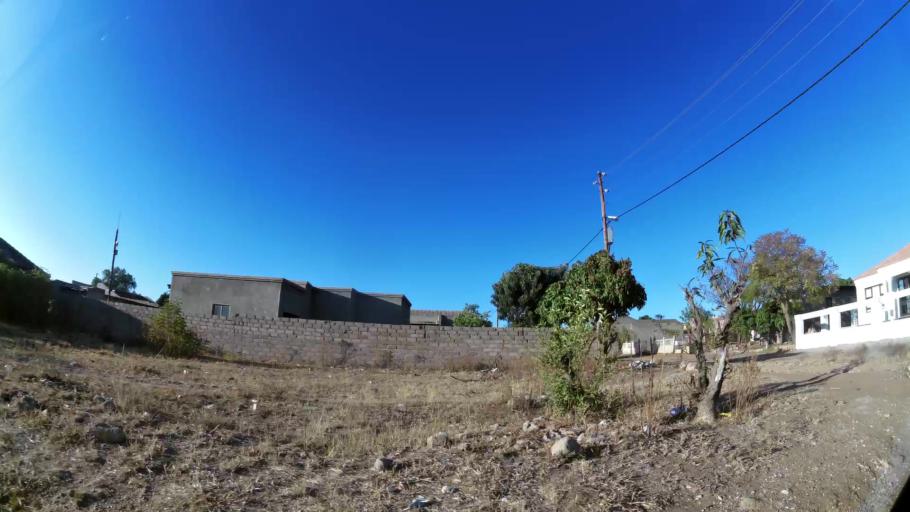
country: ZA
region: Limpopo
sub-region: Capricorn District Municipality
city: Polokwane
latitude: -23.8425
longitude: 29.3577
